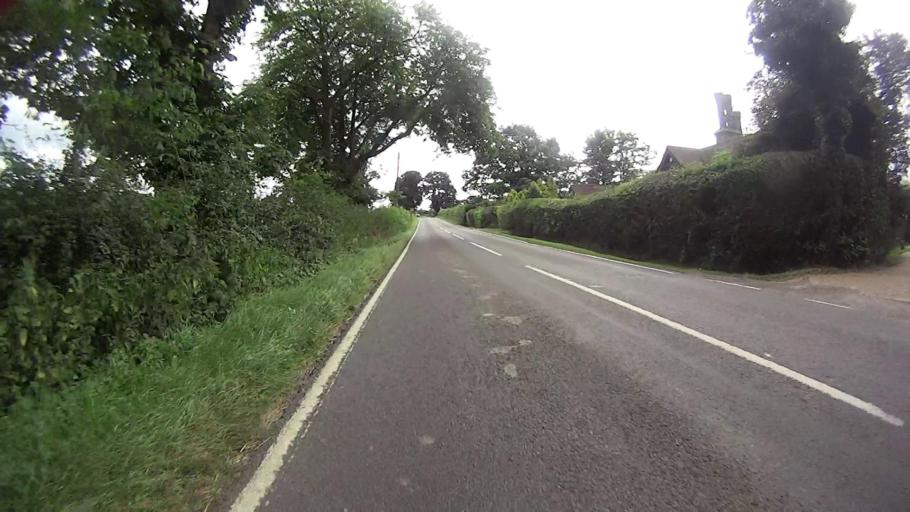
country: GB
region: England
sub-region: Surrey
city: Reigate
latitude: 51.1821
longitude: -0.2314
